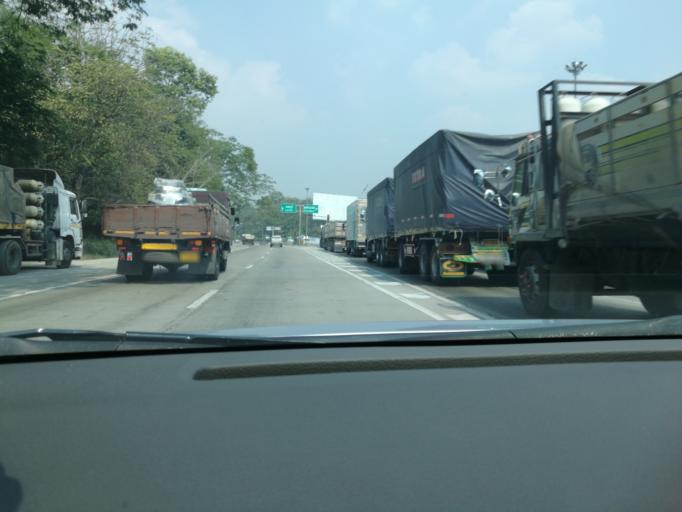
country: TH
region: Sara Buri
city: Chaloem Phra Kiat
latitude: 14.6635
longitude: 100.8872
